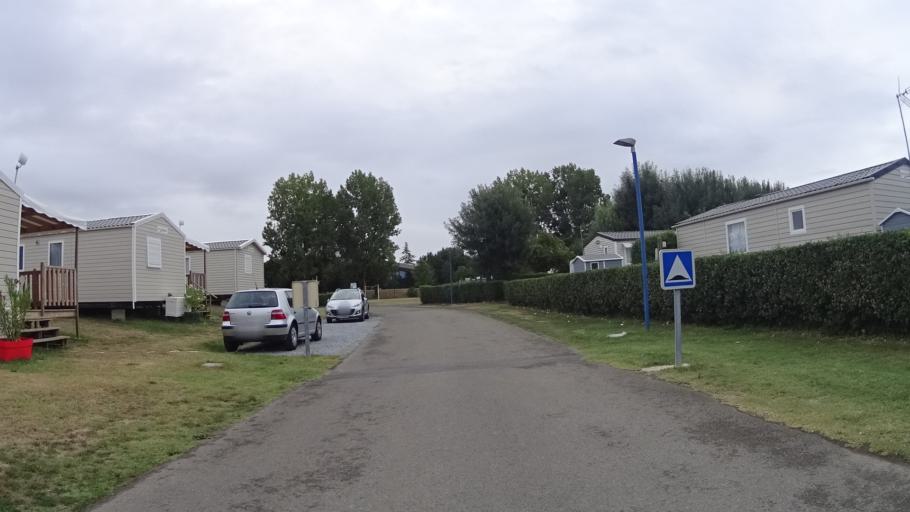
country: FR
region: Pays de la Loire
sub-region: Departement de la Loire-Atlantique
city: Saint-Gereon
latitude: 47.3615
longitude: -1.1881
